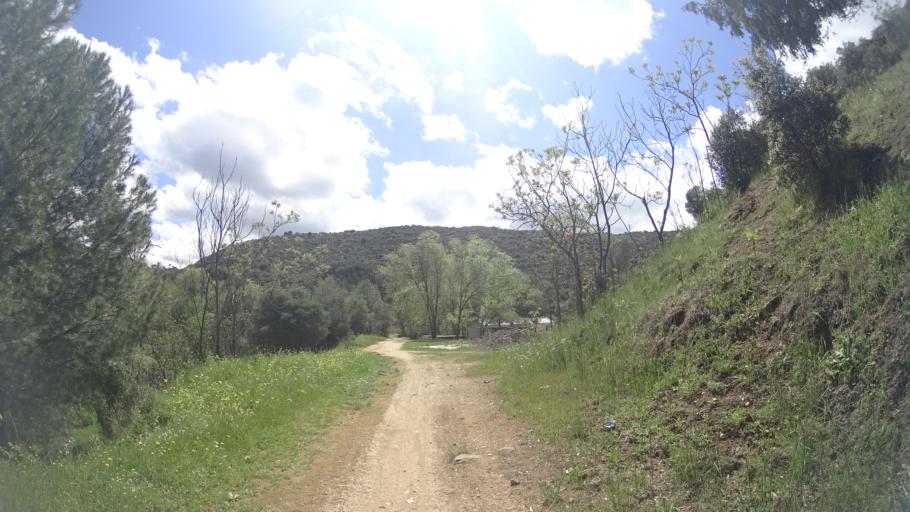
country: ES
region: Madrid
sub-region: Provincia de Madrid
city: Pelayos de la Presa
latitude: 40.3663
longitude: -4.3063
